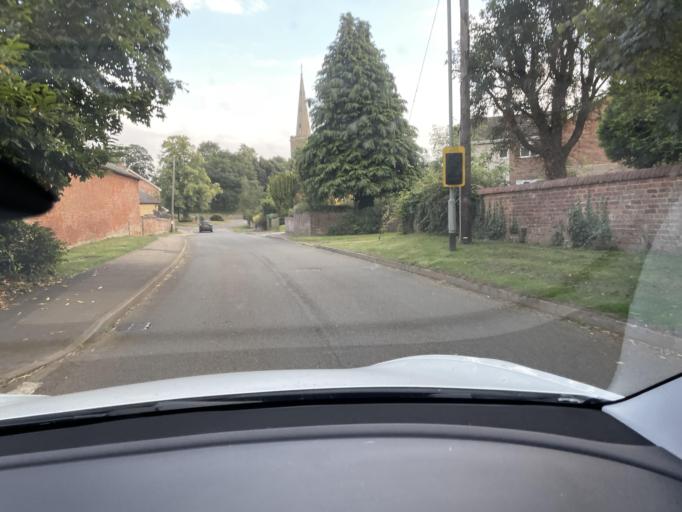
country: GB
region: England
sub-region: Leicestershire
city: Market Harborough
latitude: 52.3983
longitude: -0.9900
